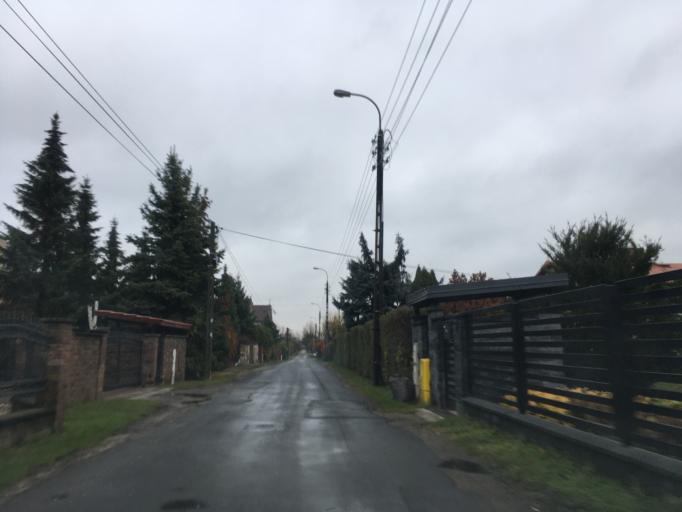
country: PL
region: Masovian Voivodeship
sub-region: Powiat grodziski
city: Podkowa Lesna
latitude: 52.1394
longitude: 20.7379
